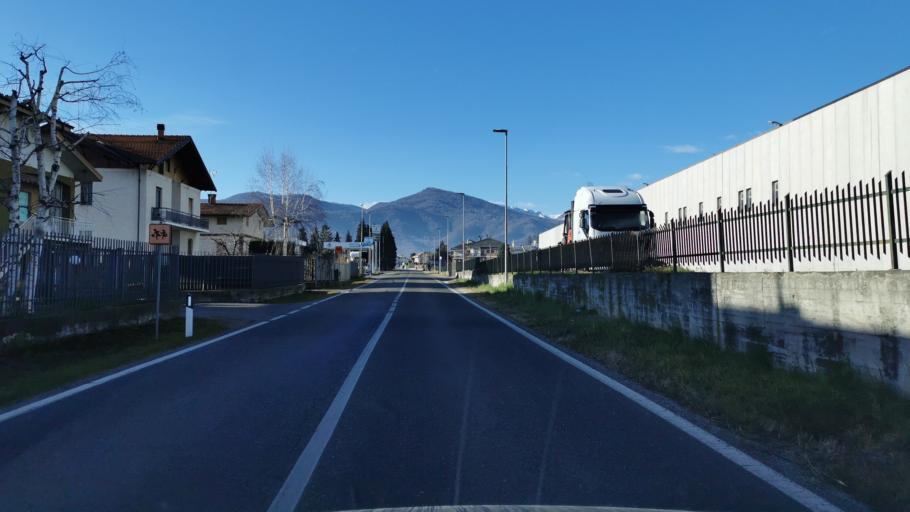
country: IT
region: Piedmont
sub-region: Provincia di Cuneo
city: Caraglio
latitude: 44.4257
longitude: 7.4428
